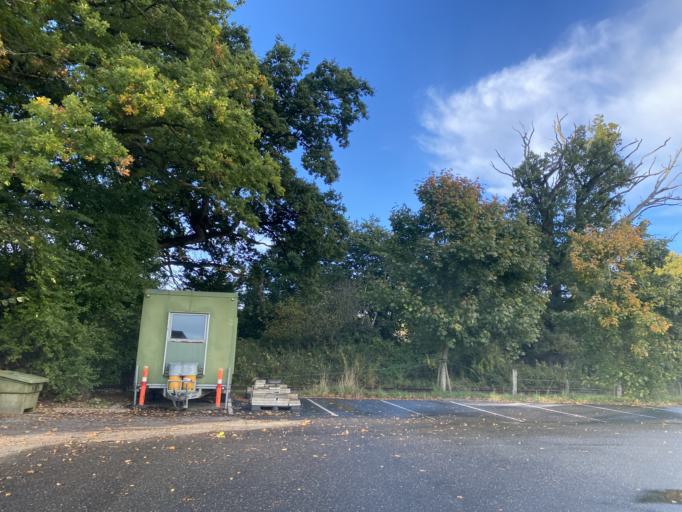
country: DK
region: South Denmark
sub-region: Haderslev Kommune
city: Haderslev
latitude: 55.2466
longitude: 9.4452
